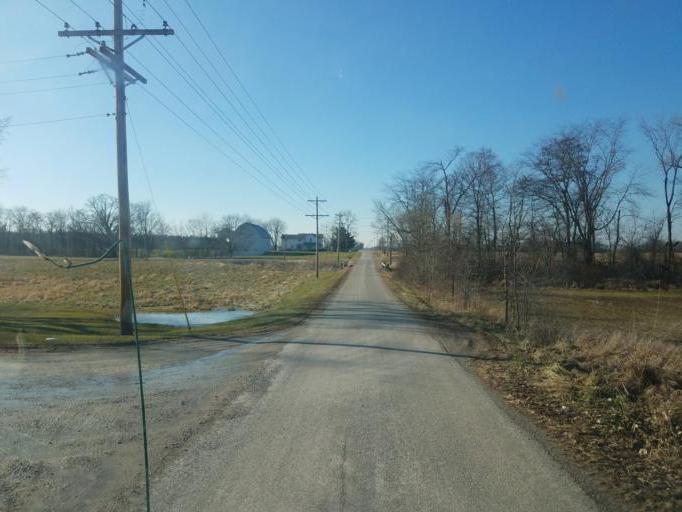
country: US
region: Ohio
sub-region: Wyandot County
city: Upper Sandusky
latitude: 40.6583
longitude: -83.3412
